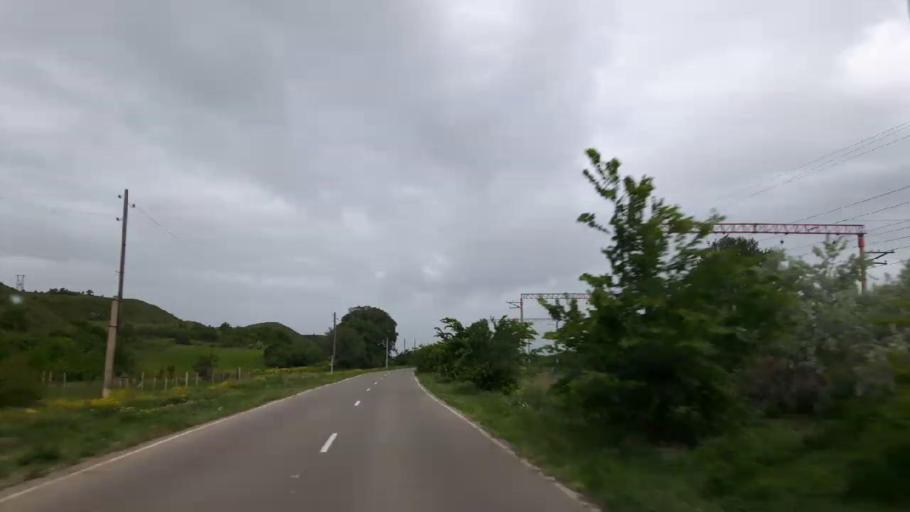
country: GE
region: Shida Kartli
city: Gori
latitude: 41.9945
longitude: 44.0272
